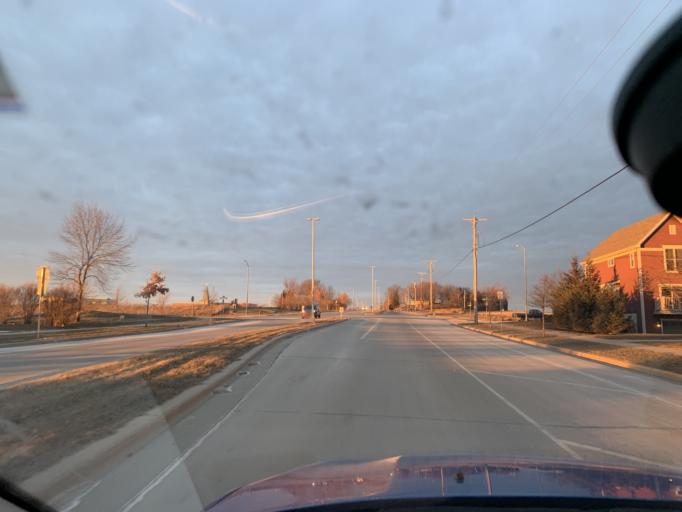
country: US
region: Wisconsin
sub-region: Dane County
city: Middleton
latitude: 43.0569
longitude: -89.5521
